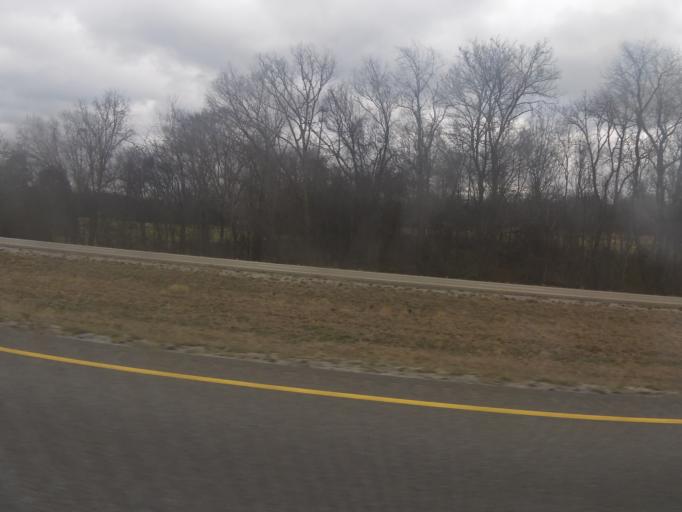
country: US
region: Tennessee
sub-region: Franklin County
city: Sewanee
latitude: 35.3384
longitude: -85.9390
